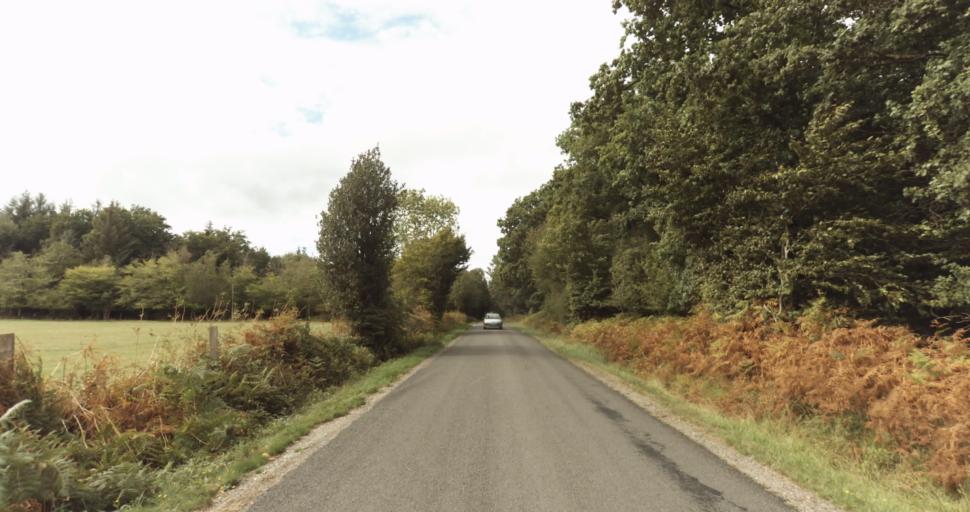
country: FR
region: Lower Normandy
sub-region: Departement de l'Orne
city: Sainte-Gauburge-Sainte-Colombe
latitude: 48.7806
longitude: 0.3871
